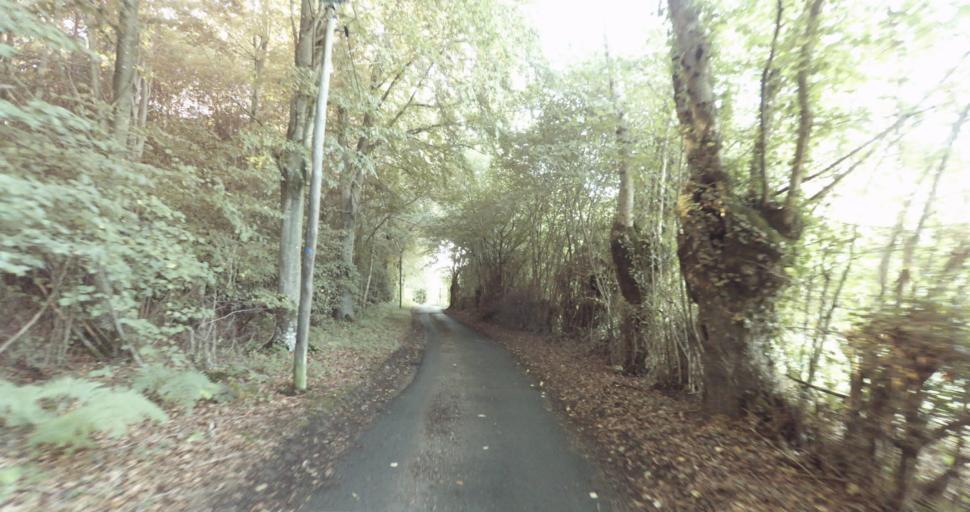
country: FR
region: Lower Normandy
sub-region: Departement de l'Orne
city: Vimoutiers
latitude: 48.8917
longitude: 0.1180
